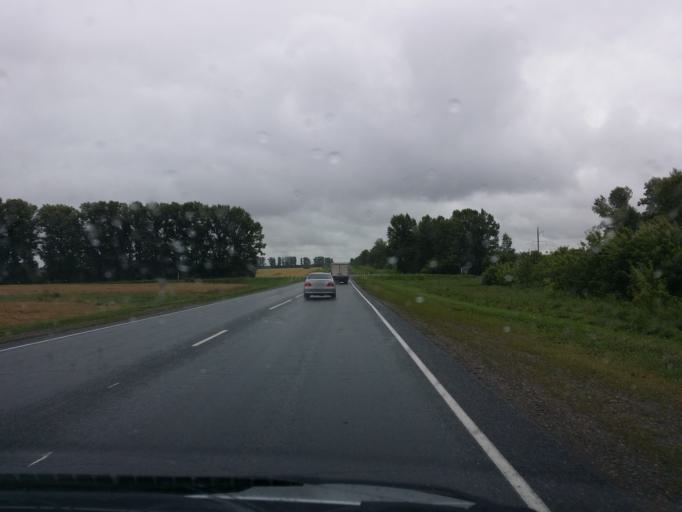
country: RU
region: Altai Krai
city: Zonal'noye
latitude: 52.7421
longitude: 84.9452
